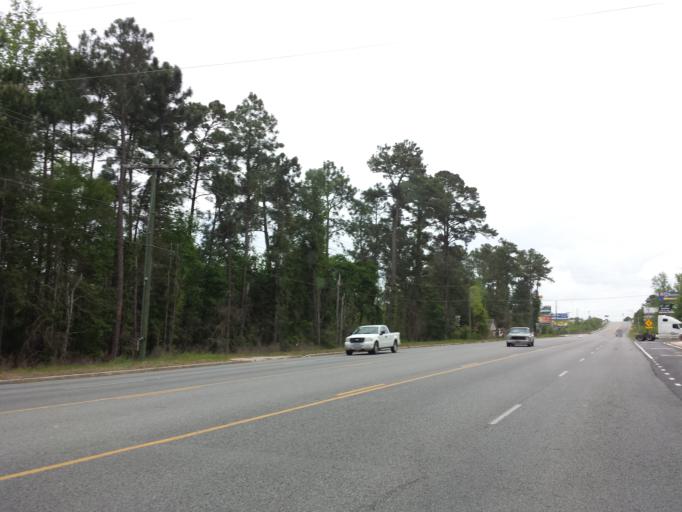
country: US
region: Georgia
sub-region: Tift County
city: Unionville
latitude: 31.4407
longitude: -83.5331
